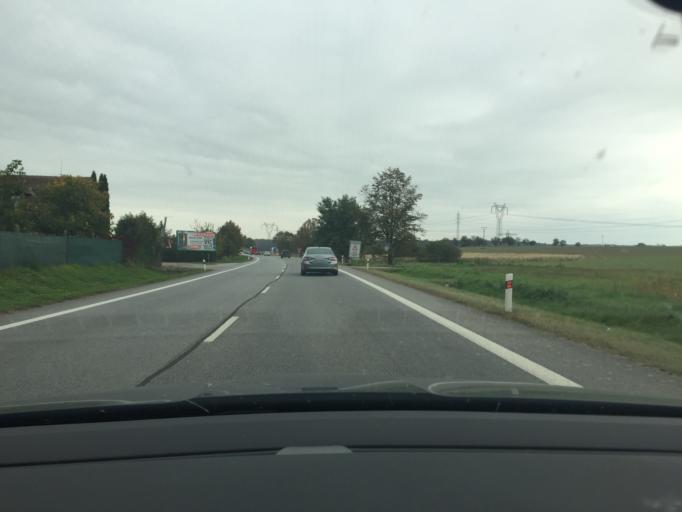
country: CZ
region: Jihocesky
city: Zliv
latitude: 49.0448
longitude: 14.3319
